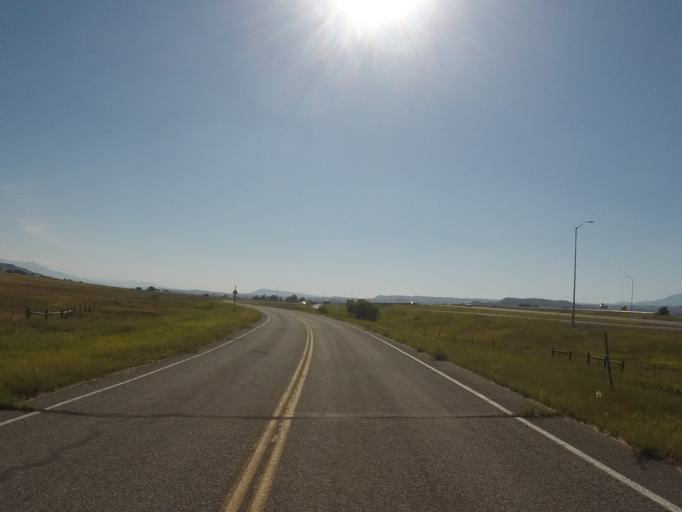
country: US
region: Montana
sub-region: Sweet Grass County
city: Big Timber
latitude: 45.8250
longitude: -109.9676
